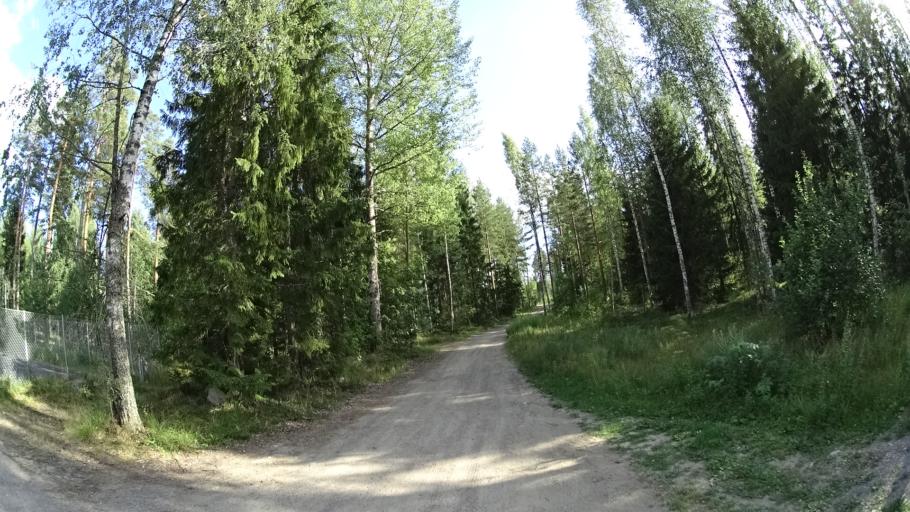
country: FI
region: Uusimaa
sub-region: Helsinki
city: Vihti
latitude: 60.3611
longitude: 24.3454
